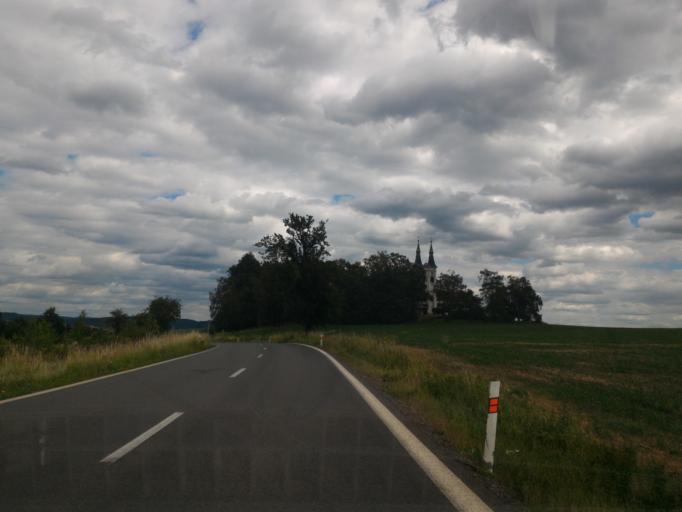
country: CZ
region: Vysocina
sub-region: Okres Jihlava
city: Telc
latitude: 49.1832
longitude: 15.4278
